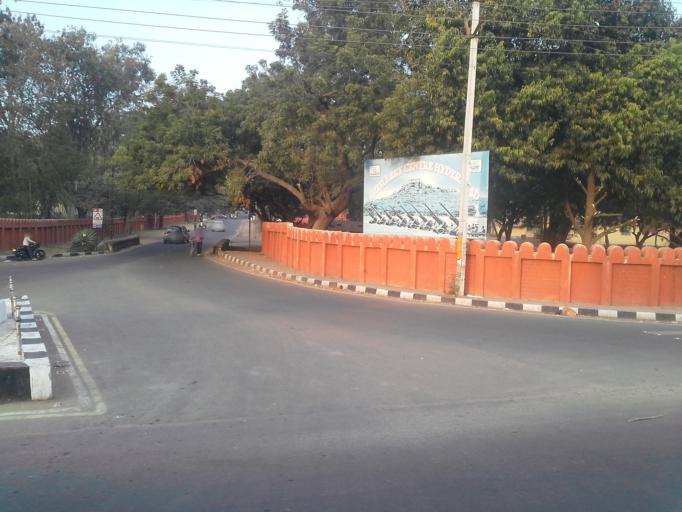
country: IN
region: Telangana
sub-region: Hyderabad
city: Hyderabad
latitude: 17.3752
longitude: 78.3966
